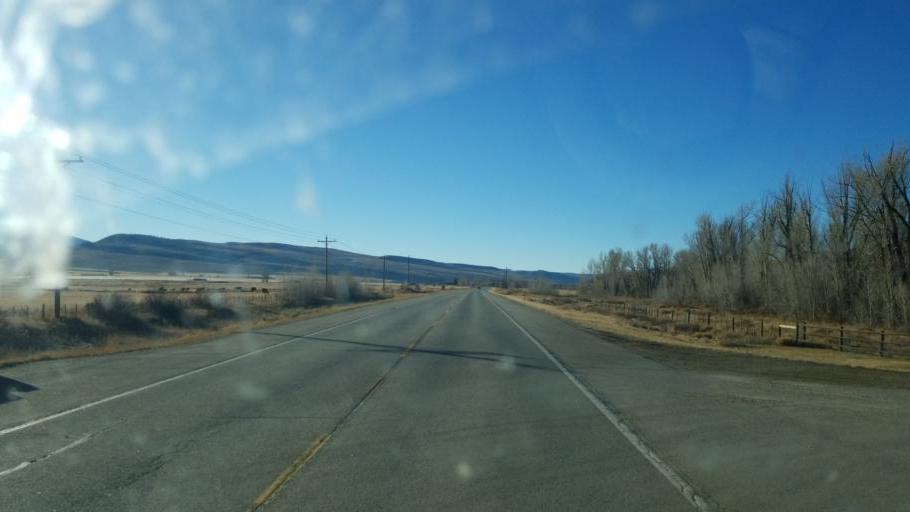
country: US
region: Colorado
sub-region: Gunnison County
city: Crested Butte
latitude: 38.7602
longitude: -106.8630
